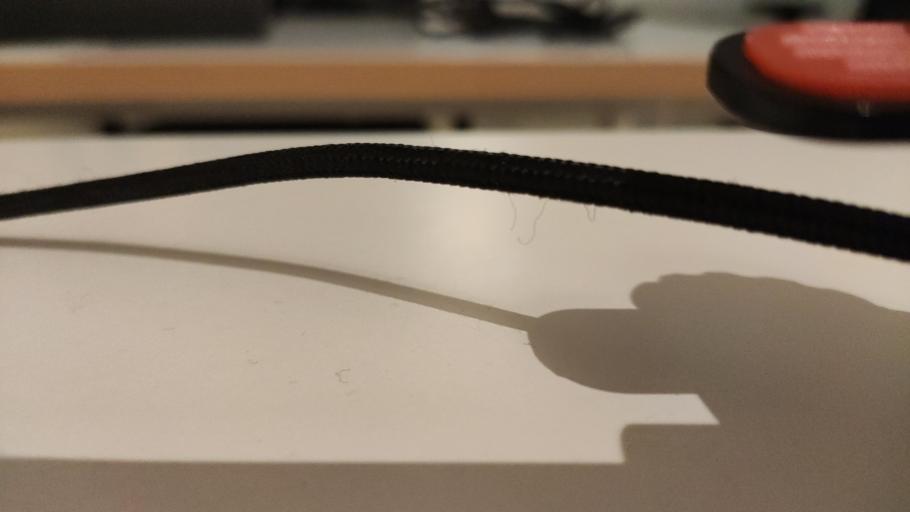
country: RU
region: Moskovskaya
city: Shaburnovo
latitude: 56.4368
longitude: 37.9183
